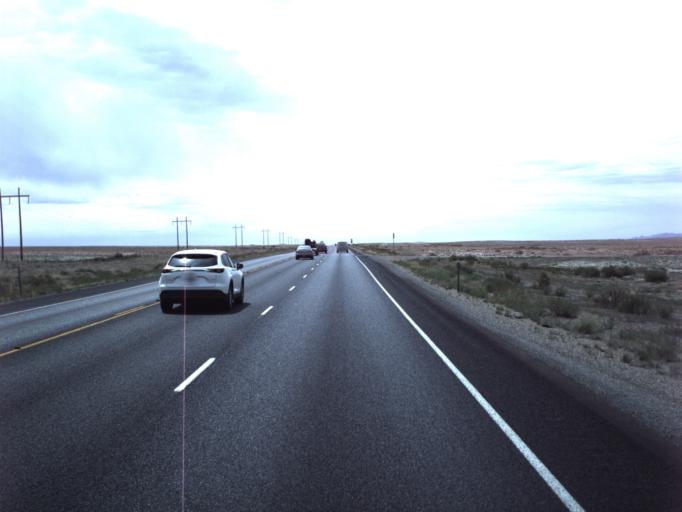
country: US
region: Utah
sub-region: Carbon County
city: East Carbon City
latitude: 39.1964
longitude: -110.3385
